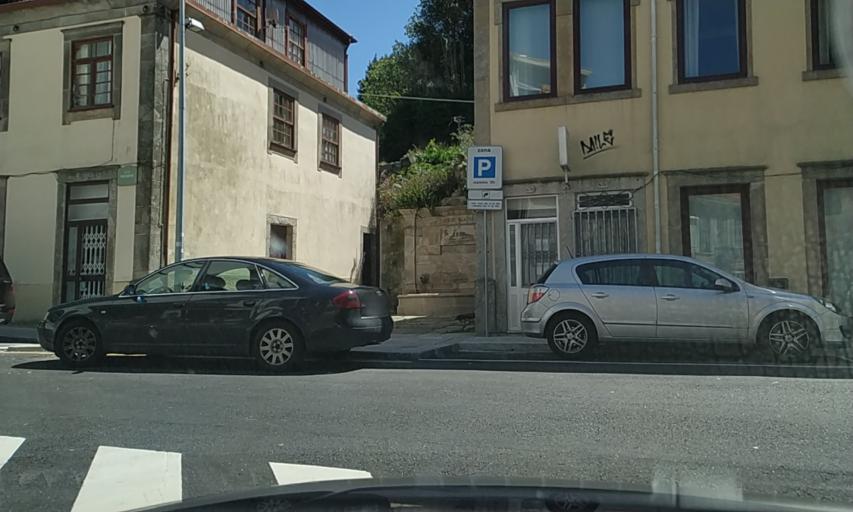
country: PT
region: Porto
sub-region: Porto
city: Porto
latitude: 41.1576
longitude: -8.6072
